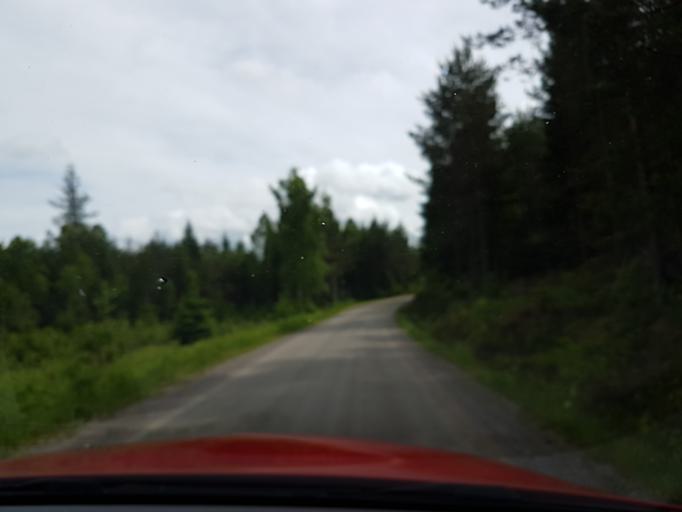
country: SE
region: Vaestra Goetaland
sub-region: Karlsborgs Kommun
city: Karlsborg
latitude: 58.7321
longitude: 14.5907
